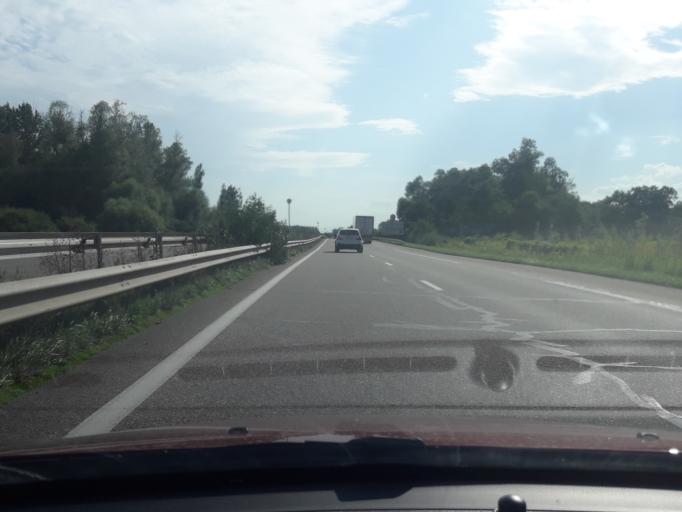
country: FR
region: Alsace
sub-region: Departement du Bas-Rhin
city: Gambsheim
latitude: 48.7144
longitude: 7.8696
